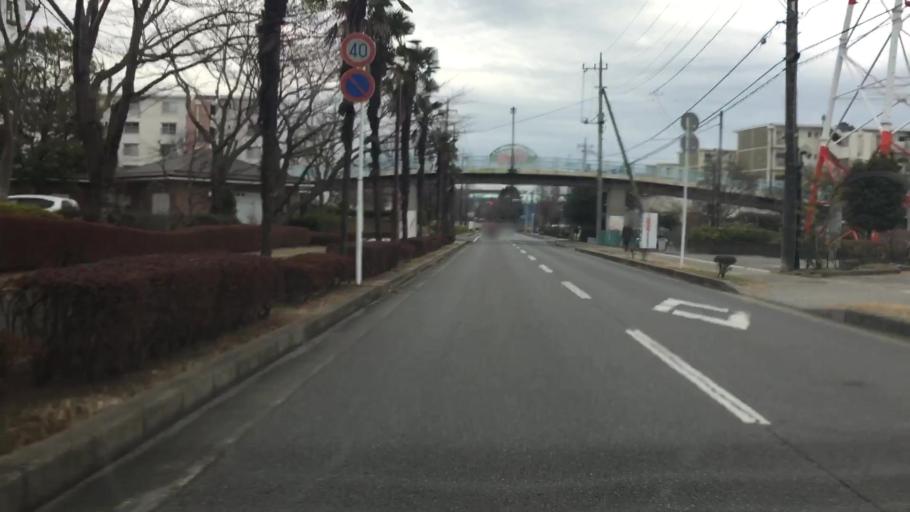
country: JP
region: Chiba
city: Shiroi
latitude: 35.8015
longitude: 140.1290
